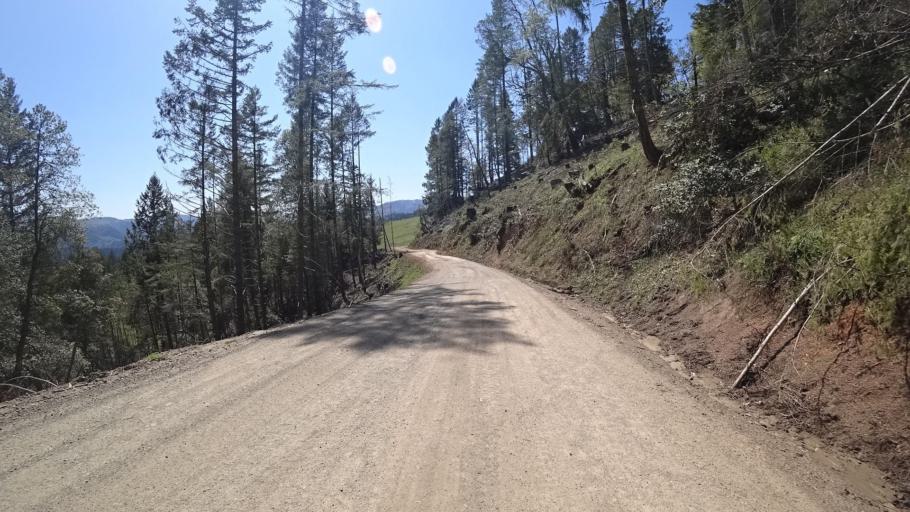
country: US
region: California
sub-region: Humboldt County
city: Redway
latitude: 40.0205
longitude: -123.6247
